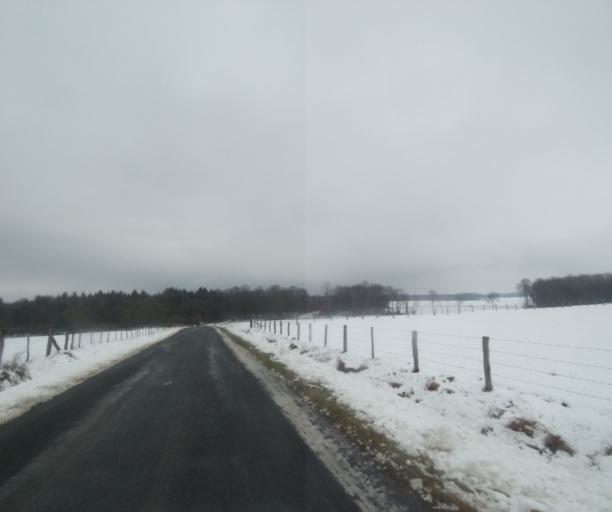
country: FR
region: Champagne-Ardenne
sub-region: Departement de la Haute-Marne
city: Montier-en-Der
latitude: 48.4691
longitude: 4.8119
